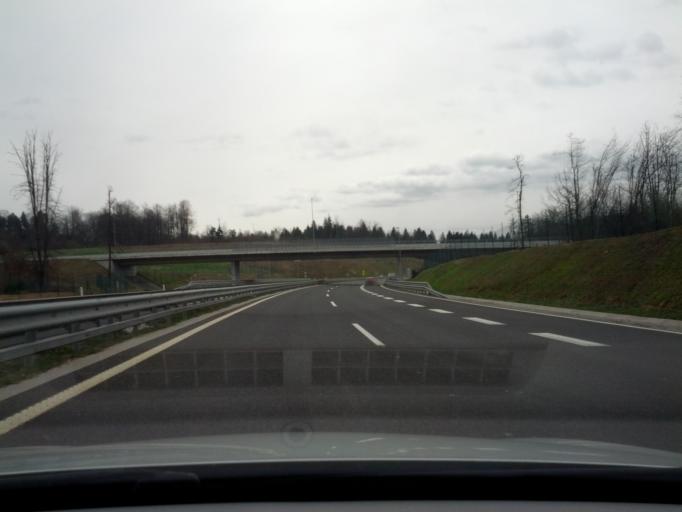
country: SI
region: Trebnje
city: Trebnje
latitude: 45.8992
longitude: 15.0533
